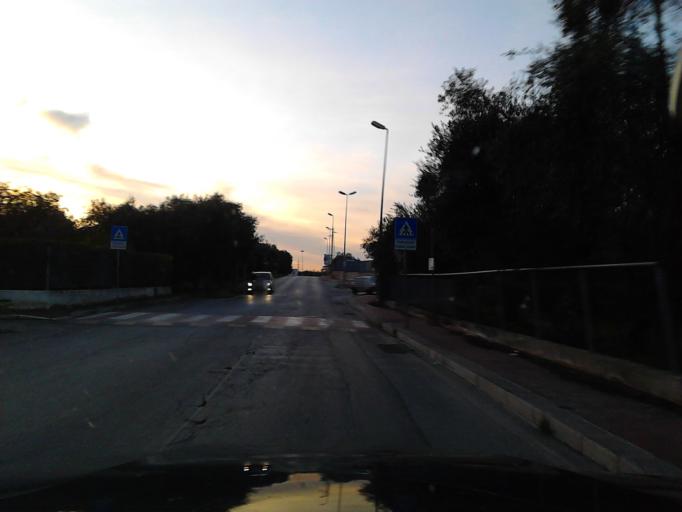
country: IT
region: Apulia
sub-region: Provincia di Bari
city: Lamie
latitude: 41.0405
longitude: 16.8758
